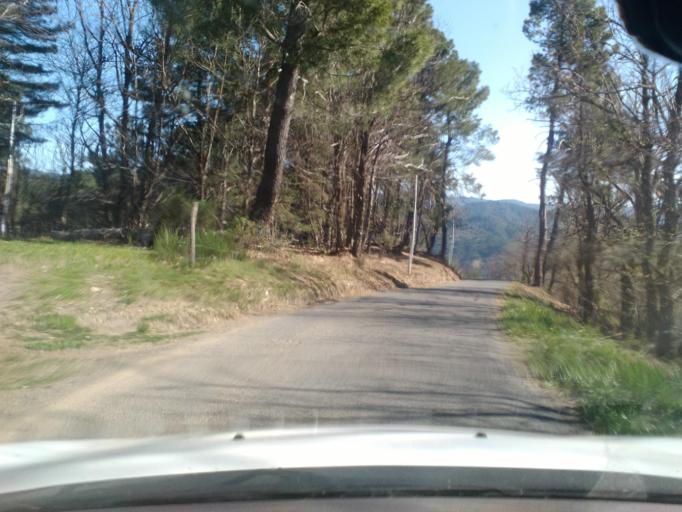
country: FR
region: Languedoc-Roussillon
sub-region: Departement du Gard
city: Saint-Jean-du-Gard
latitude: 44.1529
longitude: 3.7656
